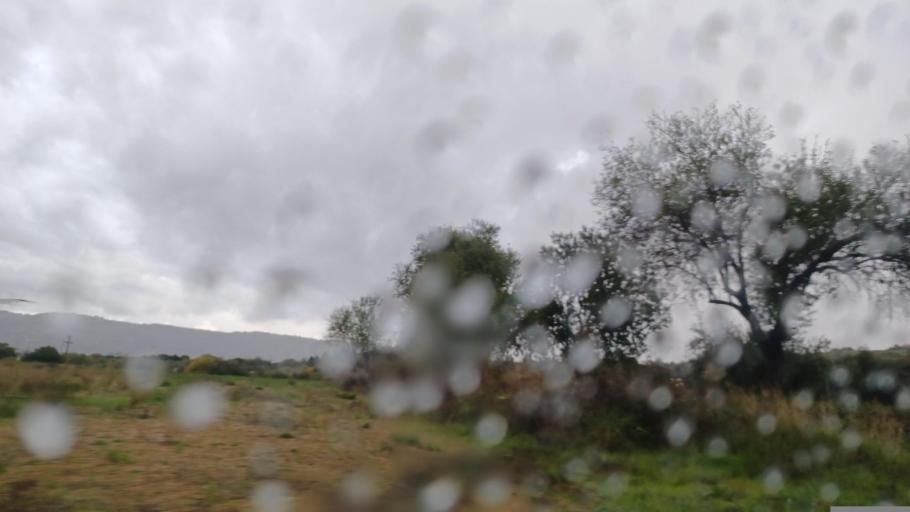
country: CY
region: Pafos
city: Mesogi
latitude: 34.8670
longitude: 32.5446
